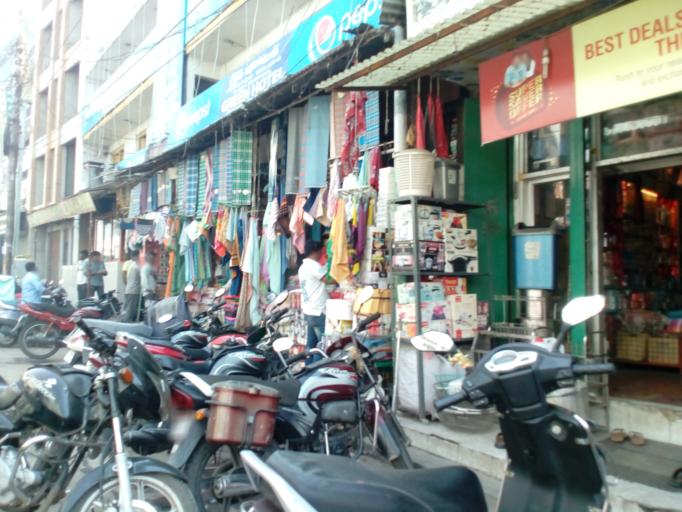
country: IN
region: Telangana
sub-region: Hyderabad
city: Malkajgiri
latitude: 17.4352
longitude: 78.4943
